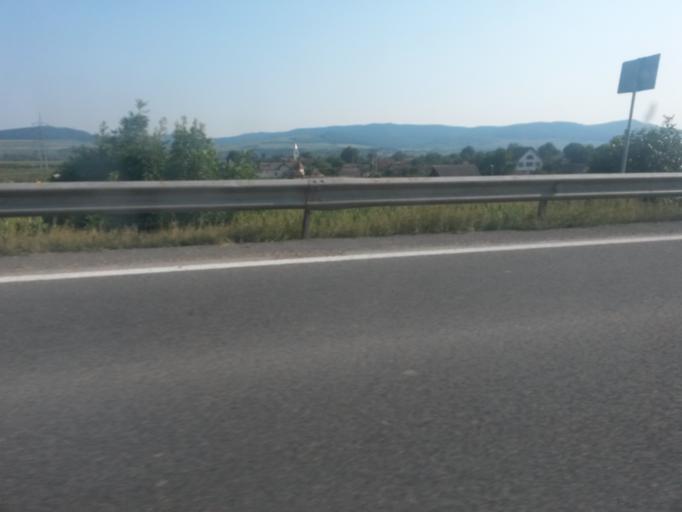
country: RO
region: Alba
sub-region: Comuna Unirea
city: Unirea
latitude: 46.3891
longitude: 23.7872
